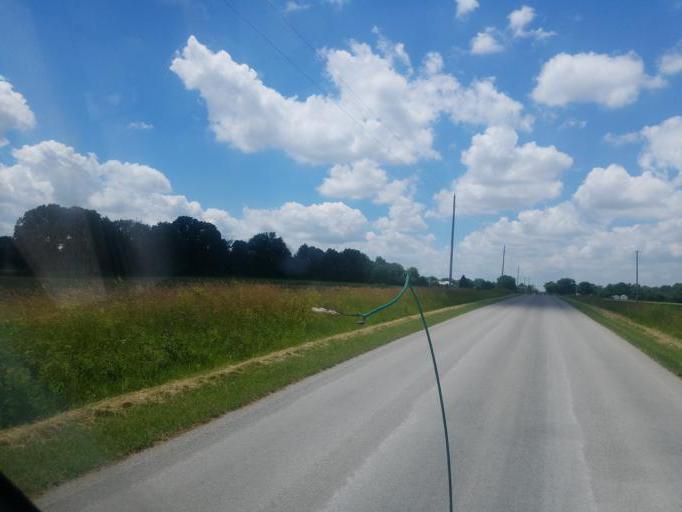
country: US
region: Ohio
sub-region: Huron County
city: Willard
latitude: 41.0791
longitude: -82.7071
